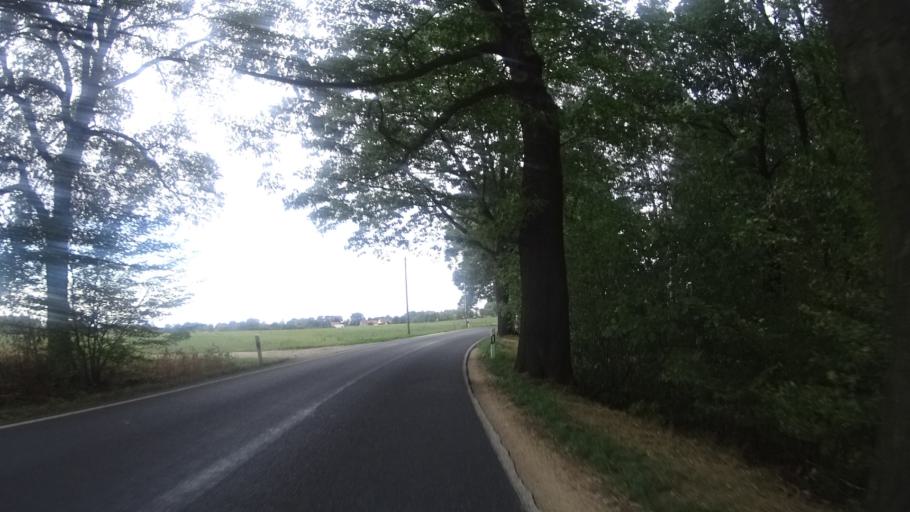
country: DE
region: Saxony
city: Rothenburg
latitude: 51.3049
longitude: 15.0046
